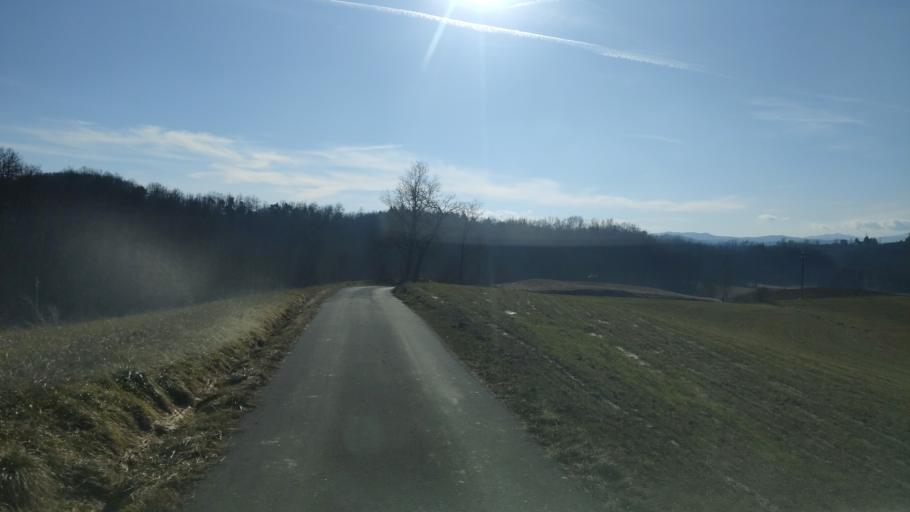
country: IT
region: Piedmont
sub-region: Provincia di Cuneo
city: Camerana
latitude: 44.4106
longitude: 8.1304
